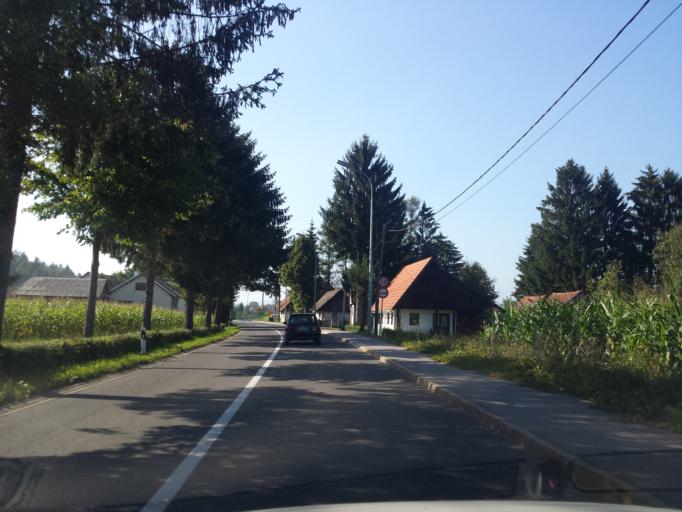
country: HR
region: Karlovacka
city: Ostarije
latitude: 45.2292
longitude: 15.2638
